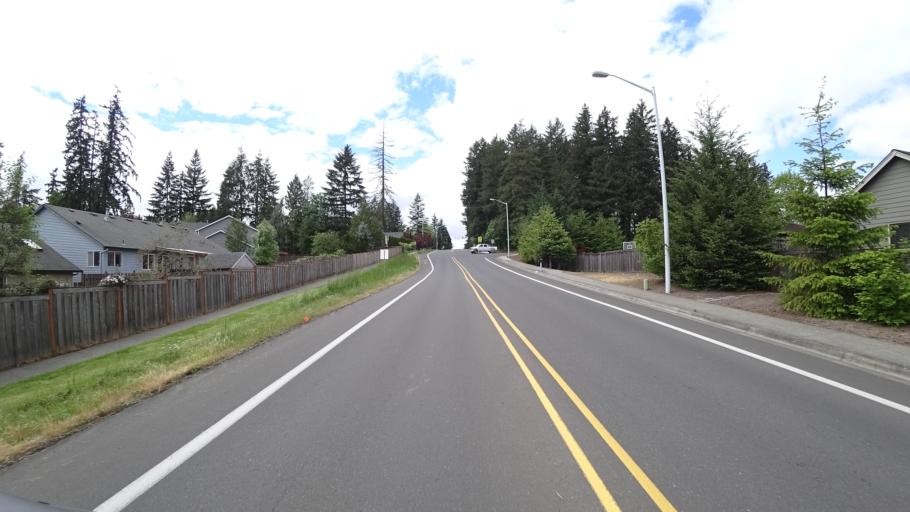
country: US
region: Oregon
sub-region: Washington County
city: Aloha
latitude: 45.4670
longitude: -122.8602
